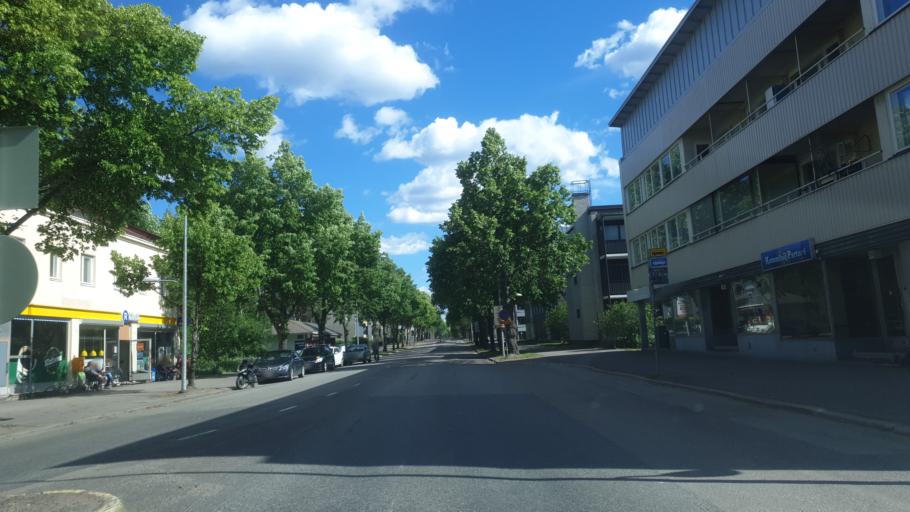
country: FI
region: Northern Savo
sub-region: Varkaus
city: Varkaus
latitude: 62.3254
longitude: 27.8950
